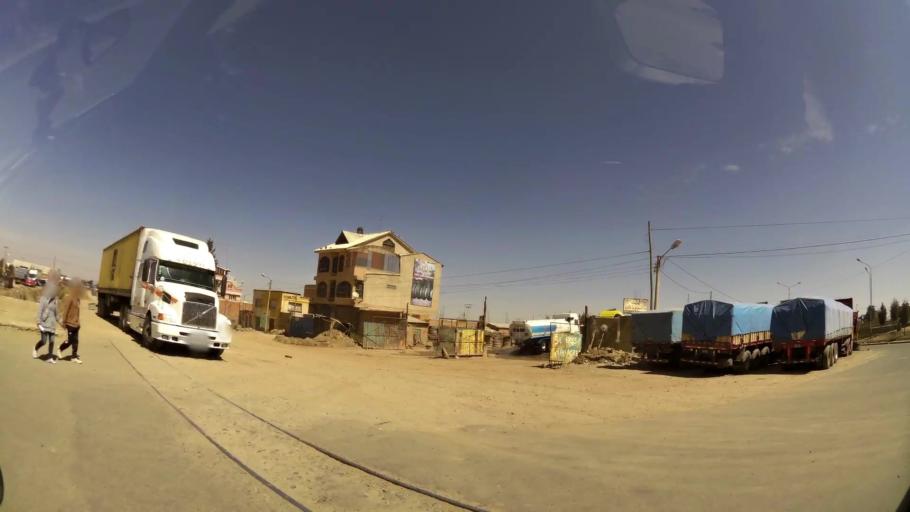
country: BO
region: La Paz
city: La Paz
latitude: -16.5459
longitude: -68.1756
